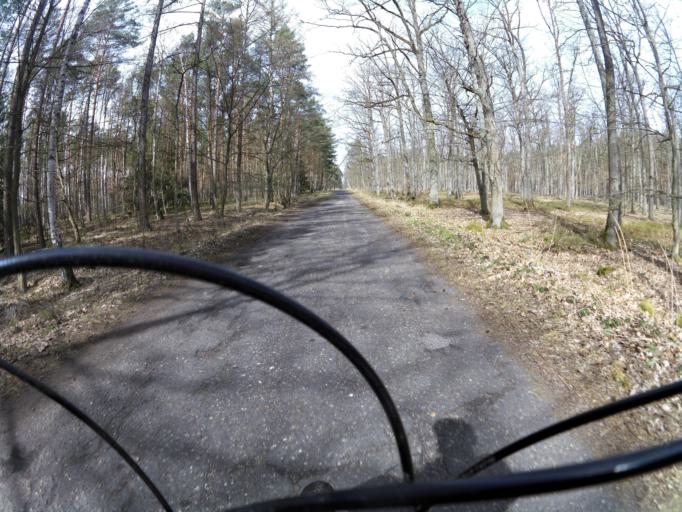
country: PL
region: West Pomeranian Voivodeship
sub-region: Powiat mysliborski
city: Boleszkowice
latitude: 52.7019
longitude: 14.5118
